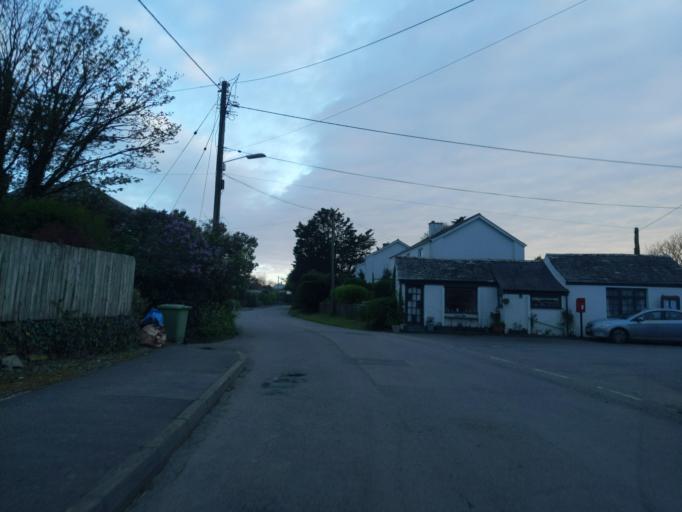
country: GB
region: England
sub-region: Cornwall
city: Polzeath
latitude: 50.5559
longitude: -4.8877
